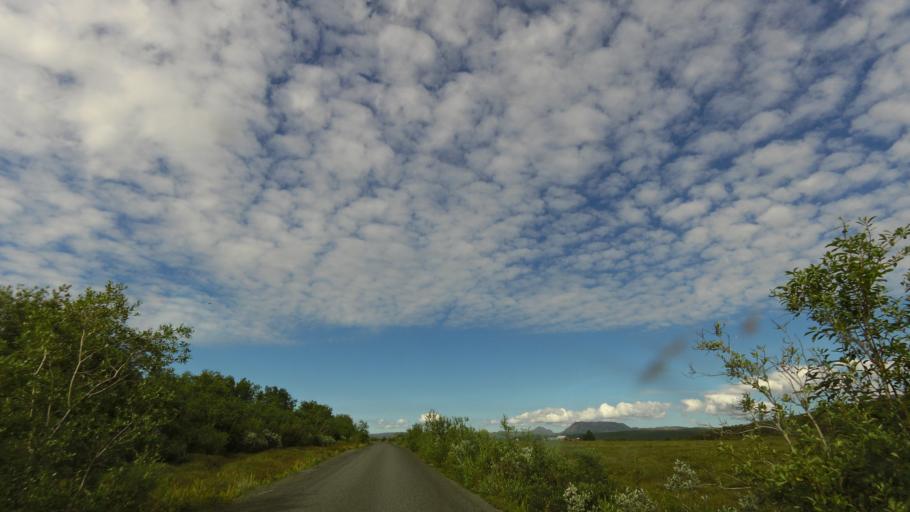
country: IS
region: Northeast
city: Husavik
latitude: 66.0229
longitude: -16.4949
